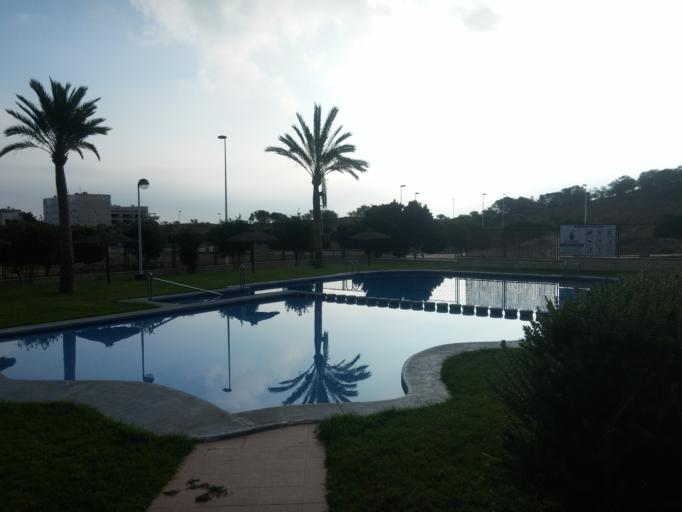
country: ES
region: Valencia
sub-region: Provincia de Alicante
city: Villajoyosa
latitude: 38.5013
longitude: -0.2441
